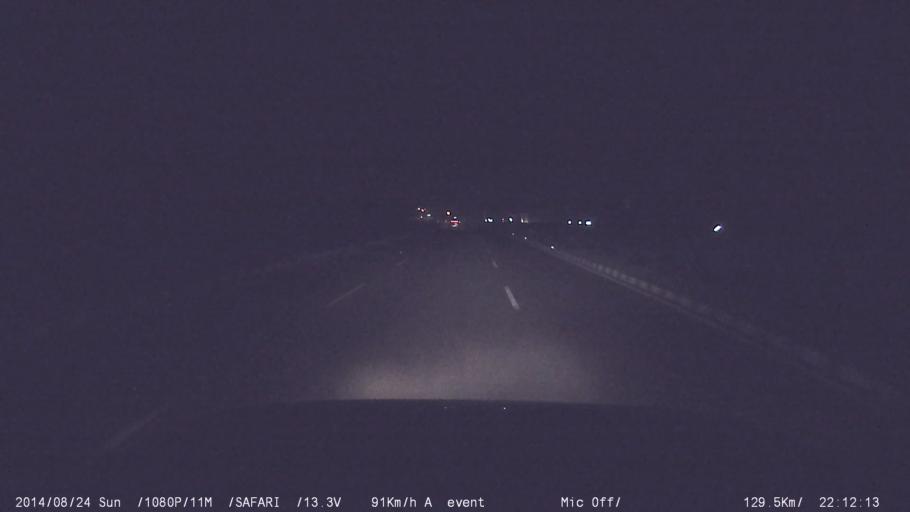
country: IN
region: Tamil Nadu
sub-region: Vellore
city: Vaniyambadi
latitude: 12.6985
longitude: 78.6417
